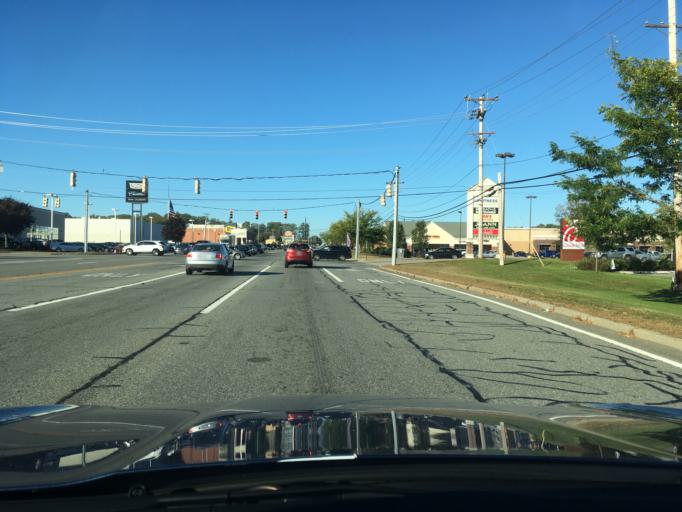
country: US
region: Rhode Island
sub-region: Kent County
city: West Warwick
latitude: 41.6985
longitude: -71.4967
